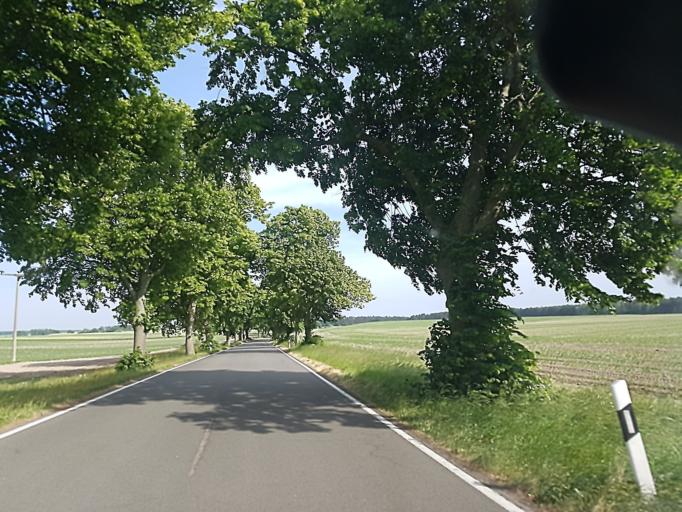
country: DE
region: Saxony-Anhalt
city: Kropstadt
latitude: 51.9804
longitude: 12.7165
